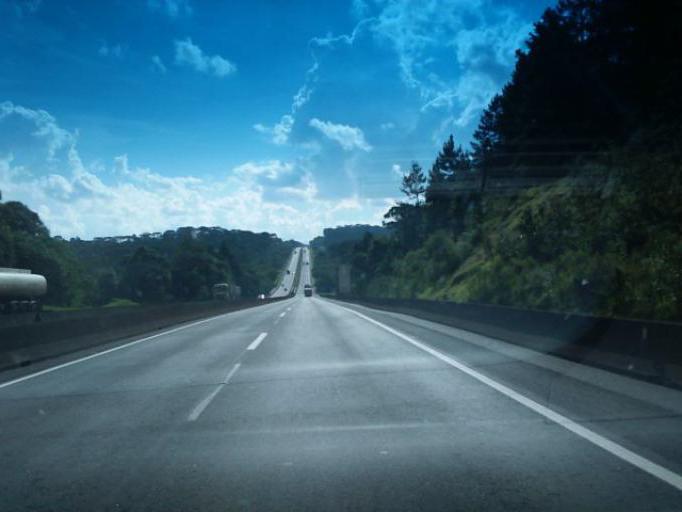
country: BR
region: Parana
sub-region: Campina Grande Do Sul
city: Campina Grande do Sul
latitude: -25.3034
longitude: -48.9662
